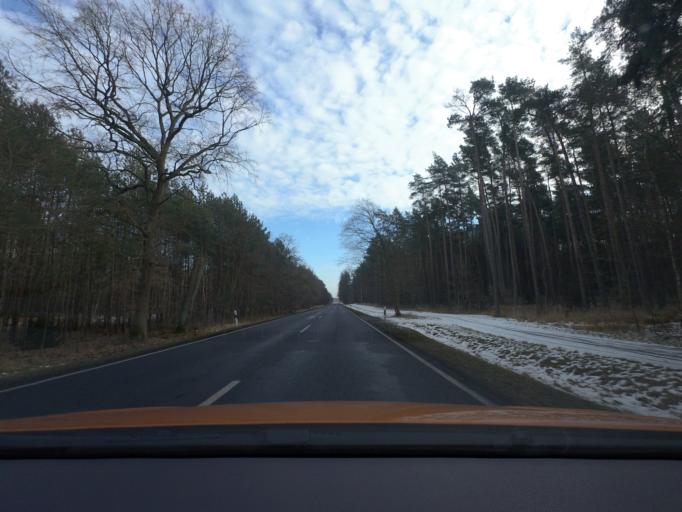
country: DE
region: Brandenburg
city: Ruthnick
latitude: 52.8976
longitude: 13.1006
